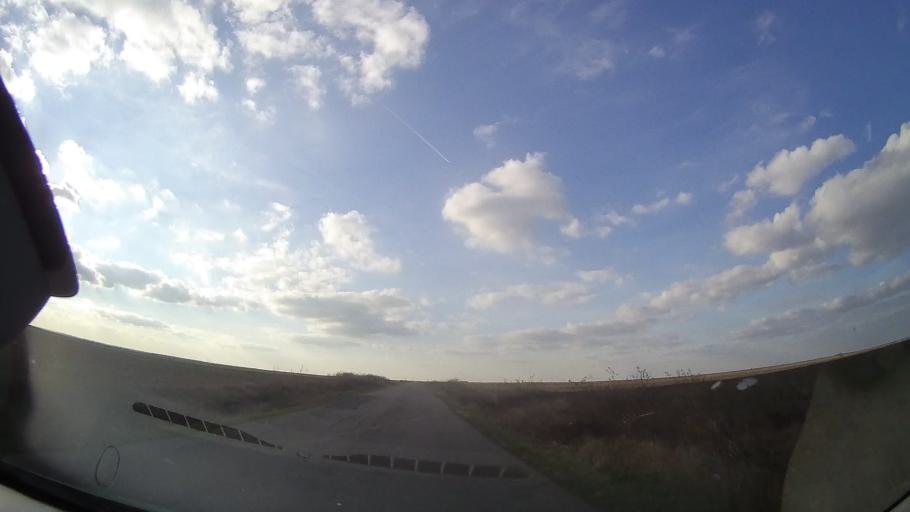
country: RO
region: Constanta
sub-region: Comuna Cerchezu
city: Cerchezu
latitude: 43.8242
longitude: 28.1409
